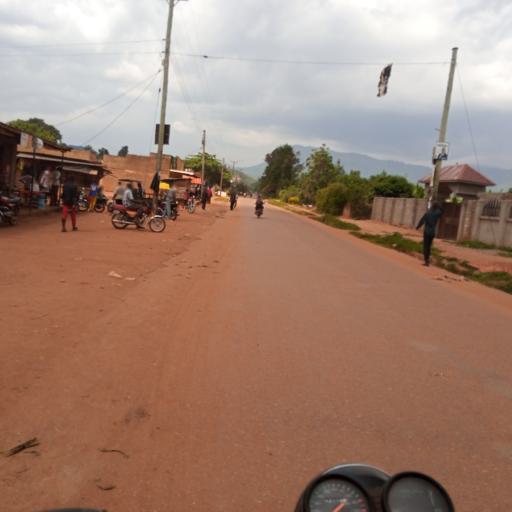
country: UG
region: Eastern Region
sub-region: Mbale District
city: Mbale
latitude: 1.0984
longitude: 34.1773
